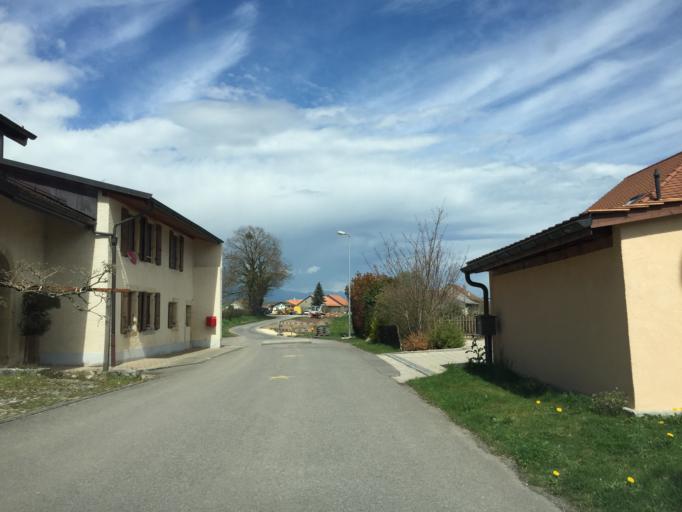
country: CH
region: Vaud
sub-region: Morges District
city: La Chaux
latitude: 46.6189
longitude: 6.4739
